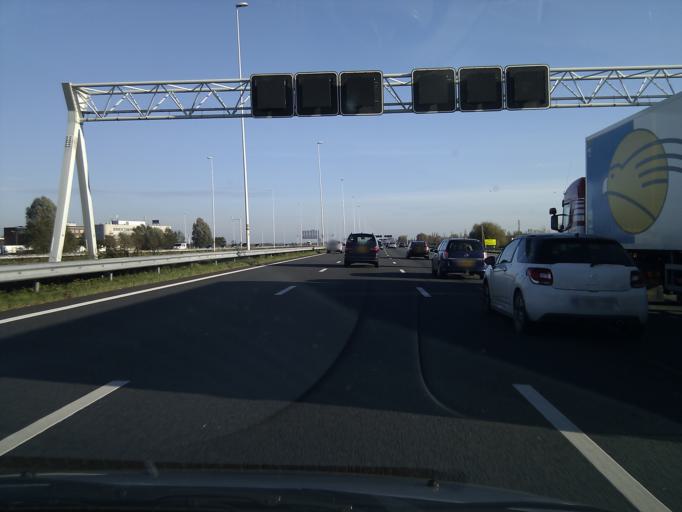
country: NL
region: South Holland
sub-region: Bodegraven-Reeuwijk
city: Bodegraven
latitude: 52.0668
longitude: 4.7574
